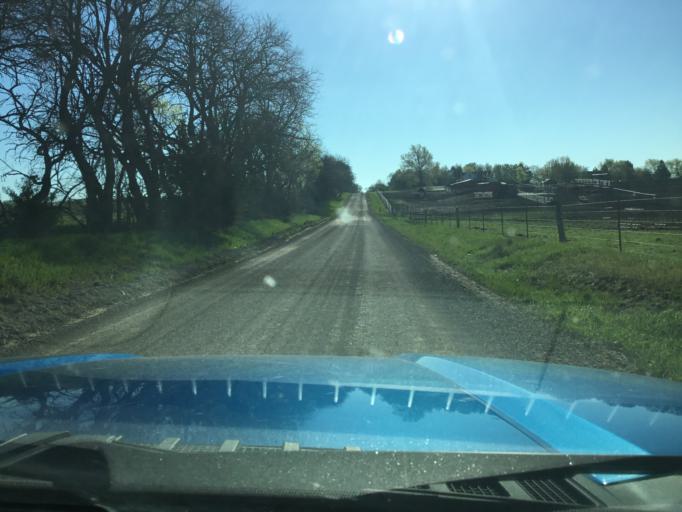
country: US
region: Kansas
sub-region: Douglas County
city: Lawrence
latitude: 38.9569
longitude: -95.3698
